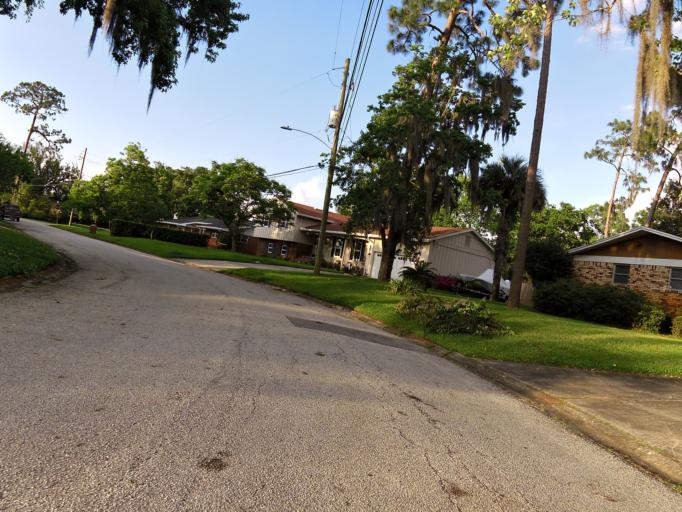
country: US
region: Florida
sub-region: Clay County
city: Orange Park
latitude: 30.2233
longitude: -81.6141
